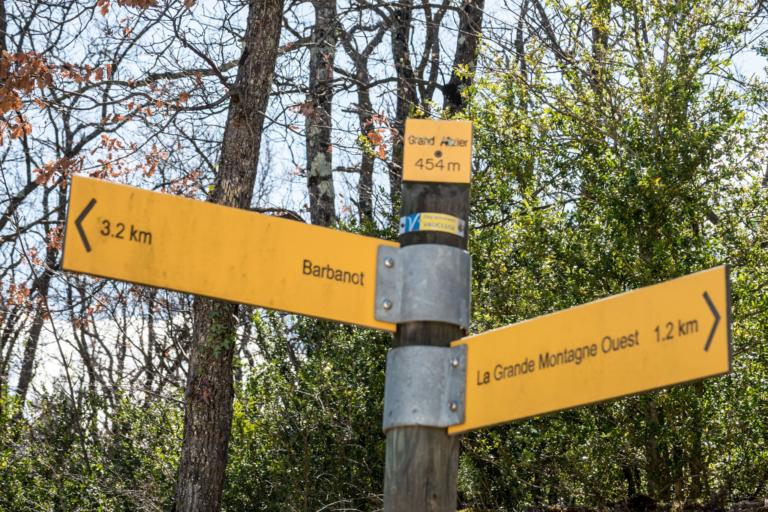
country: FR
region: Provence-Alpes-Cote d'Azur
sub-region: Departement du Vaucluse
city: Vaison-la-Romaine
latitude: 44.1998
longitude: 5.0597
